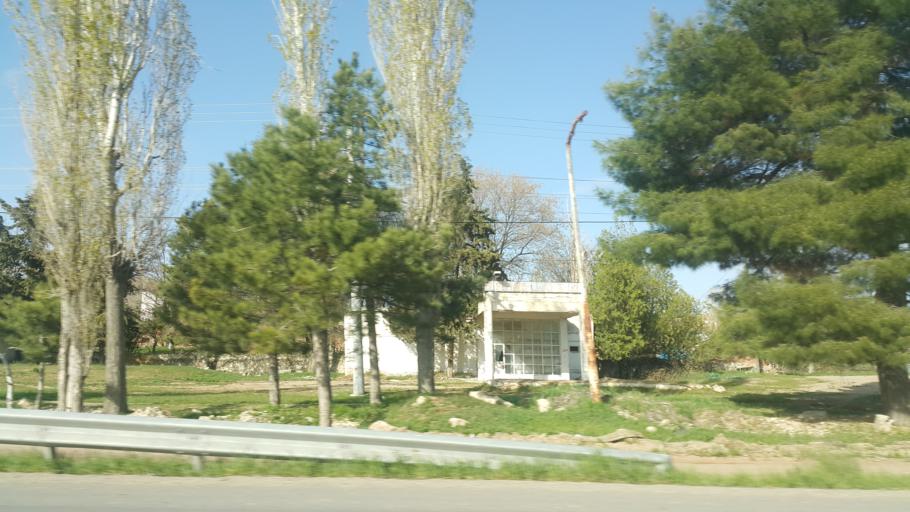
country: TR
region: Aksaray
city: Acipinar
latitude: 38.5235
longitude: 33.8430
